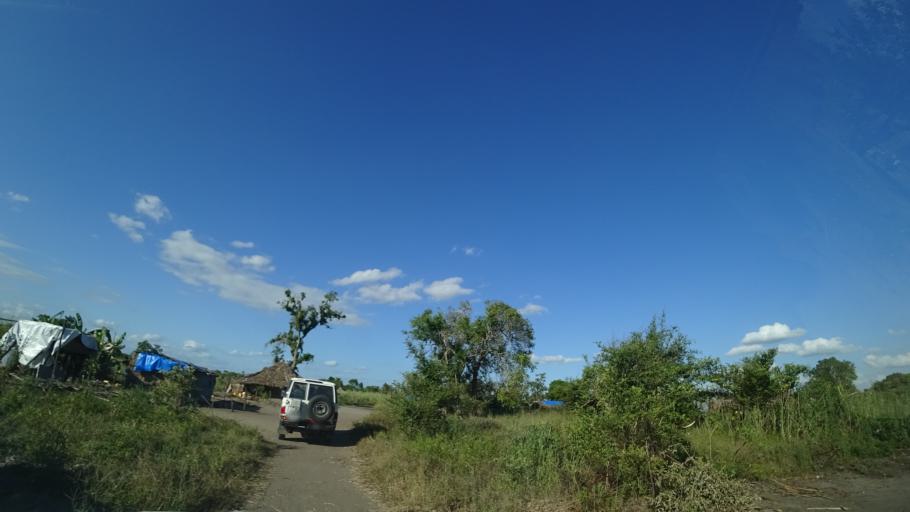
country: MZ
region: Sofala
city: Dondo
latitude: -19.3543
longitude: 34.5891
